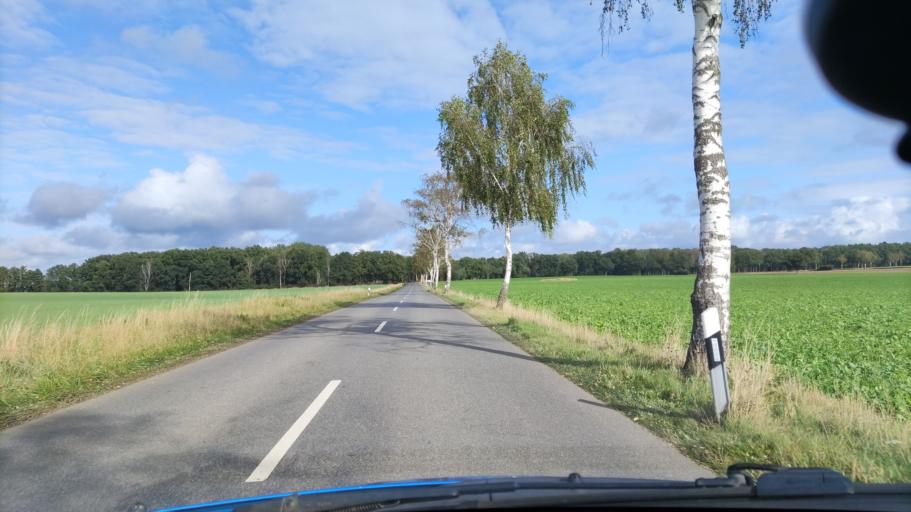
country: DE
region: Lower Saxony
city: Romstedt
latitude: 53.0882
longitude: 10.6740
